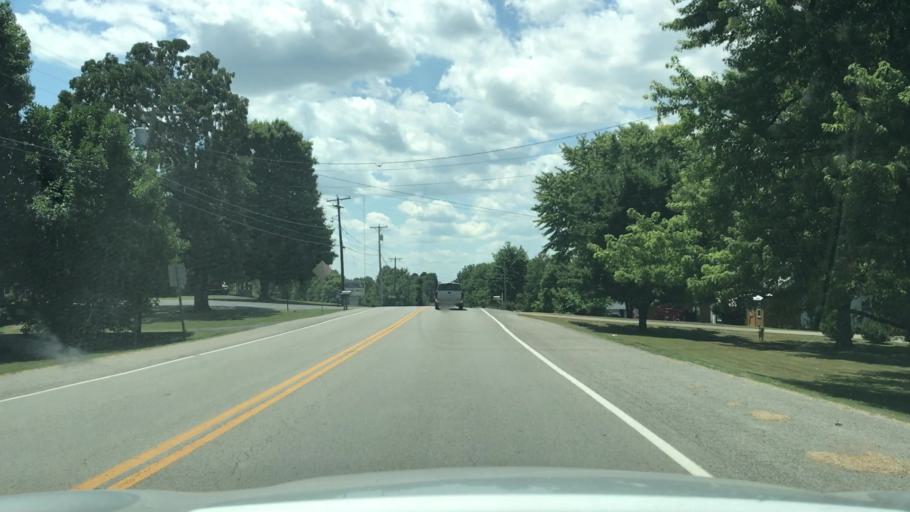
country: US
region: Kentucky
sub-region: Muhlenberg County
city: Greenville
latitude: 37.1991
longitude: -87.2070
